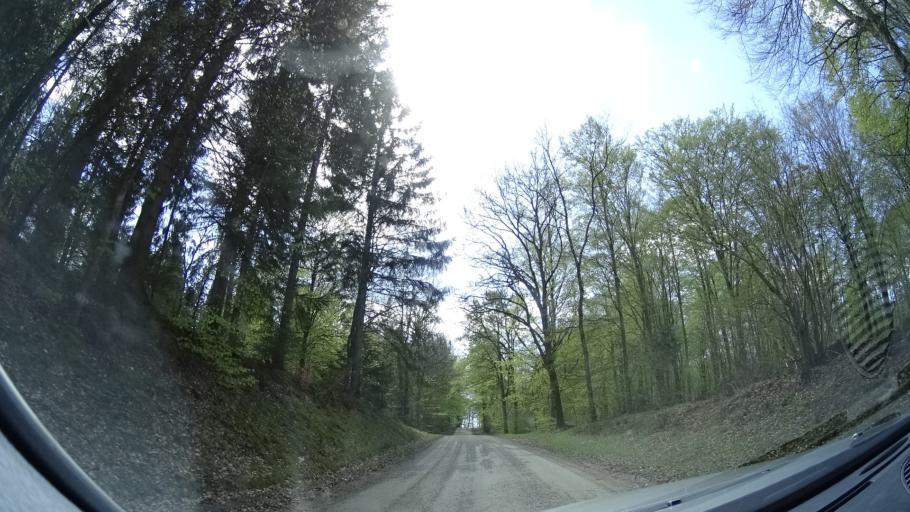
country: SE
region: Skane
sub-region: Hassleholms Kommun
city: Tormestorp
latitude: 56.0912
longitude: 13.7132
